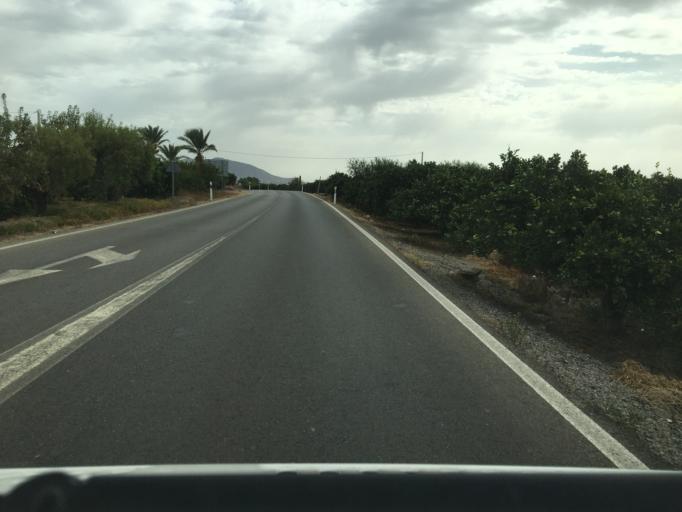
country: ES
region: Andalusia
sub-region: Provincia de Almeria
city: Huercal-Overa
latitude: 37.4092
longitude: -1.9227
